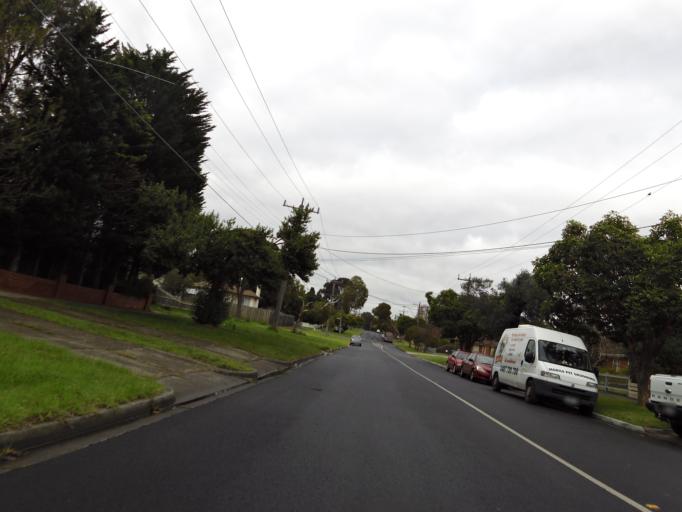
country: AU
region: Victoria
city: Heidelberg West
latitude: -37.7419
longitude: 145.0368
